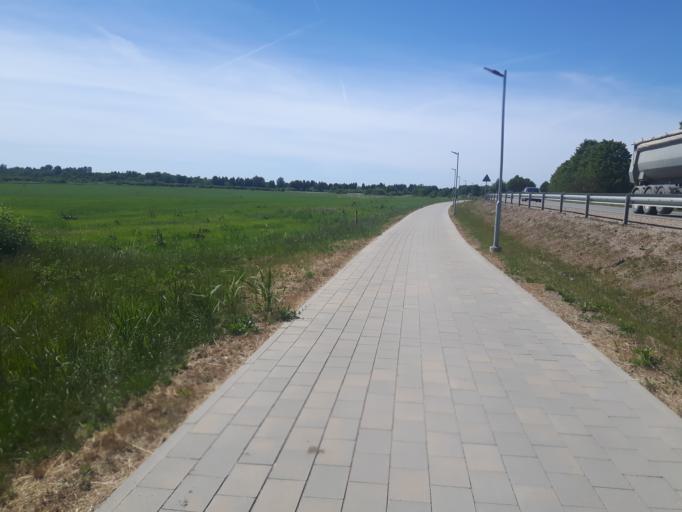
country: LV
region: Grobina
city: Grobina
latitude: 56.5325
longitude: 21.1174
